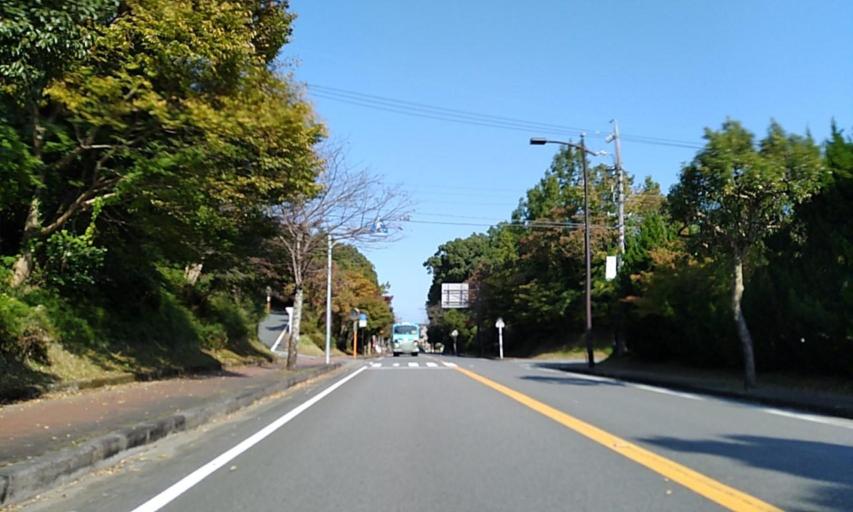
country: JP
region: Mie
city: Ise
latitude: 34.4708
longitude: 136.7260
